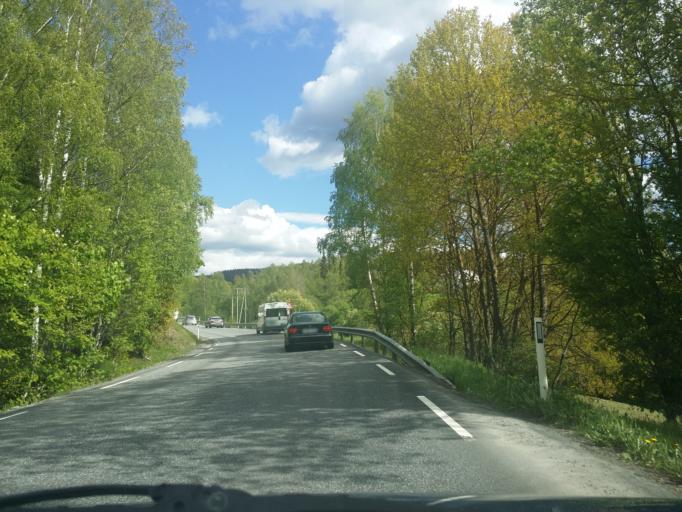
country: NO
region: Oppland
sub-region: Jevnaker
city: Jevnaker
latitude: 60.2662
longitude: 10.4856
